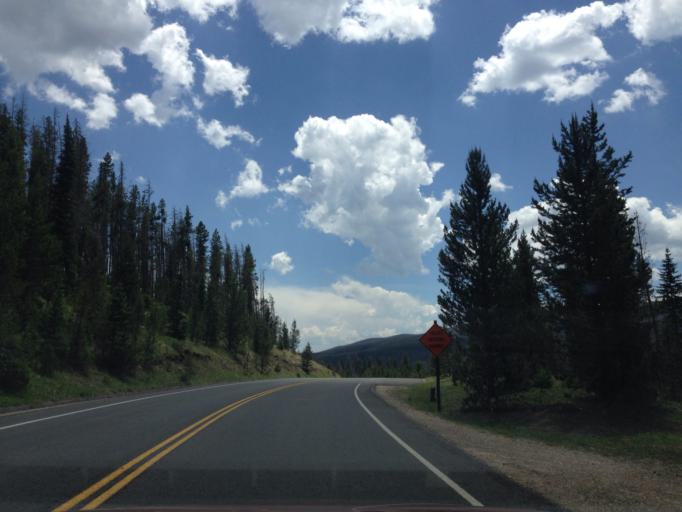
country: US
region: Colorado
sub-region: Grand County
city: Granby
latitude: 40.3412
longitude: -105.8567
